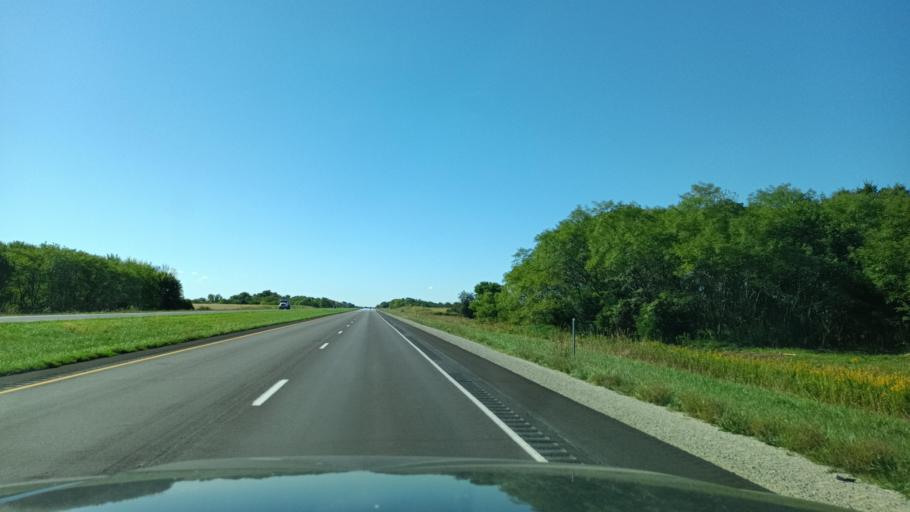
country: US
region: Illinois
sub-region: Hancock County
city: Nauvoo
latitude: 40.4890
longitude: -91.4445
